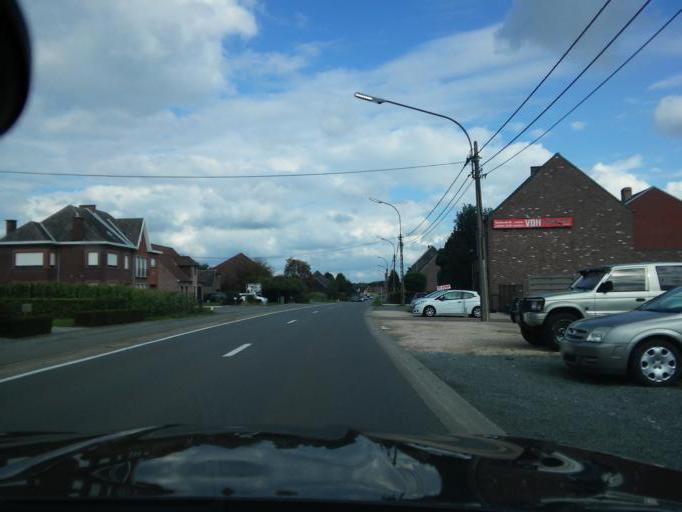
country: BE
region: Flanders
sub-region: Provincie Oost-Vlaanderen
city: Geraardsbergen
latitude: 50.8067
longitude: 3.9183
